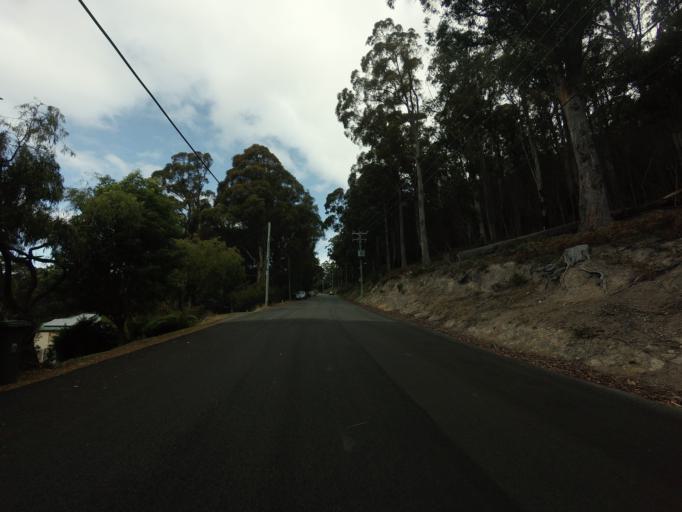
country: AU
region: Tasmania
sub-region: Hobart
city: Dynnyrne
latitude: -42.9089
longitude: 147.2669
